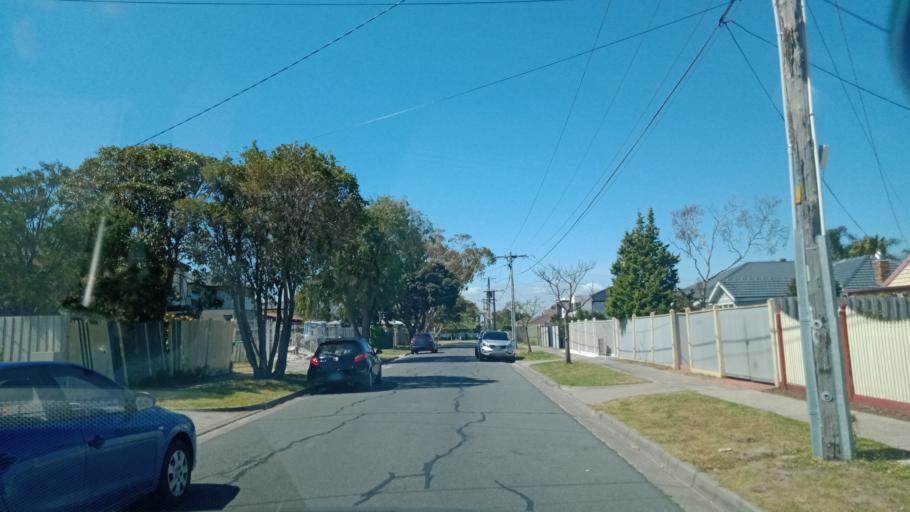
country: AU
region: Victoria
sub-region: Kingston
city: Bonbeach
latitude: -38.0553
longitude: 145.1273
